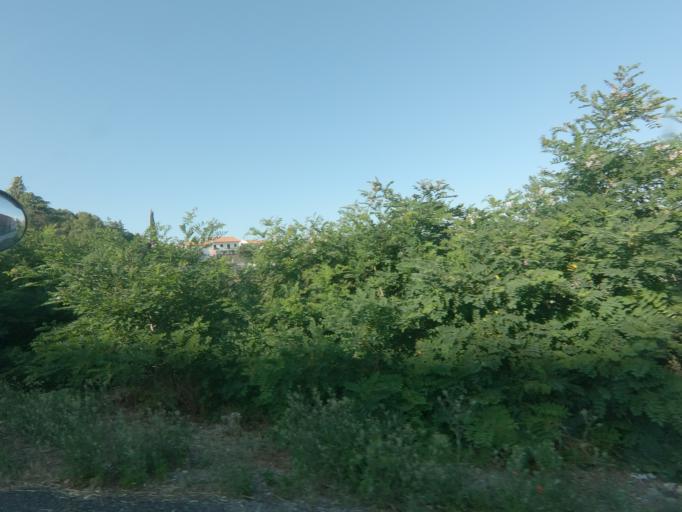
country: PT
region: Vila Real
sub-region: Sabrosa
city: Vilela
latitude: 41.1835
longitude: -7.6073
